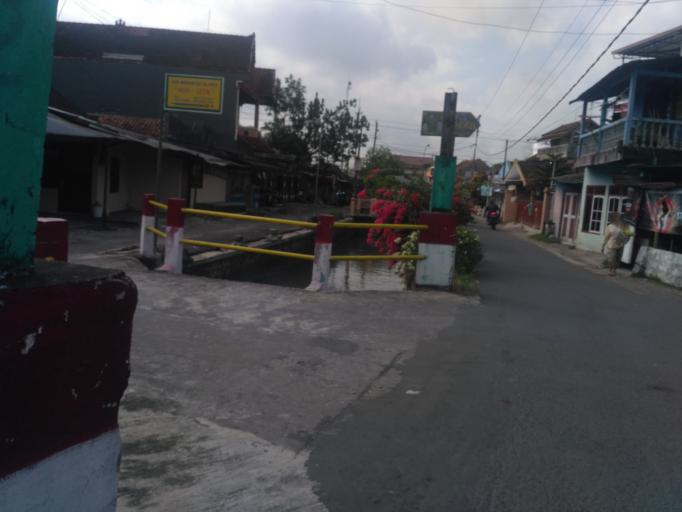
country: ID
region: Daerah Istimewa Yogyakarta
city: Yogyakarta
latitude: -7.7611
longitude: 110.3610
